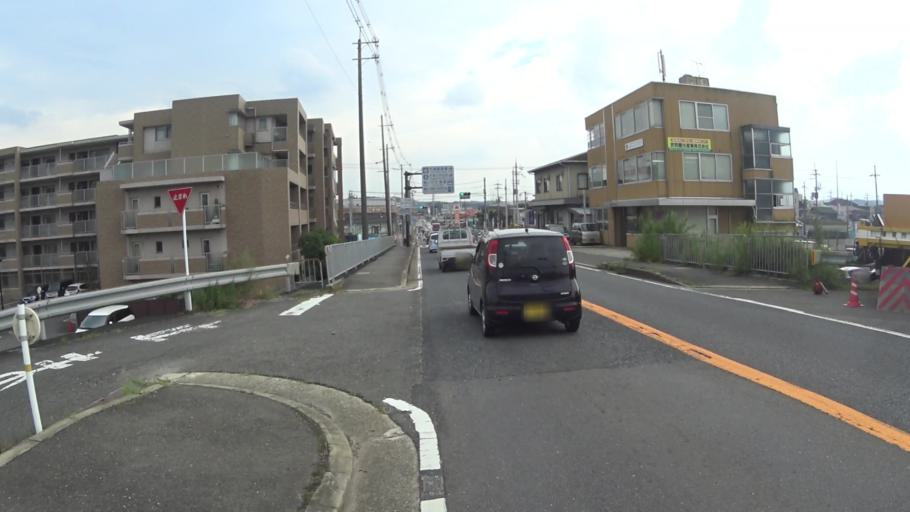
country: JP
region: Nara
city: Nara-shi
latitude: 34.7381
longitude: 135.8229
